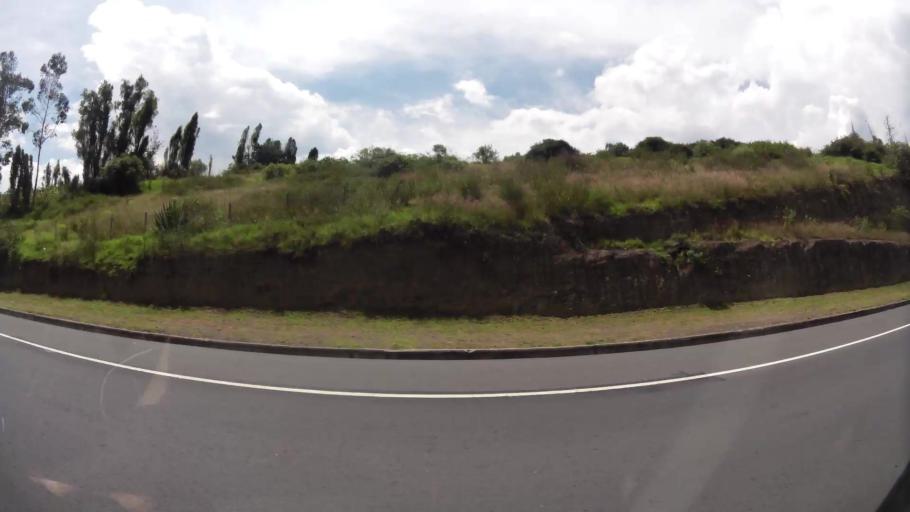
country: EC
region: Pichincha
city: Sangolqui
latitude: -0.1820
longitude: -78.3401
